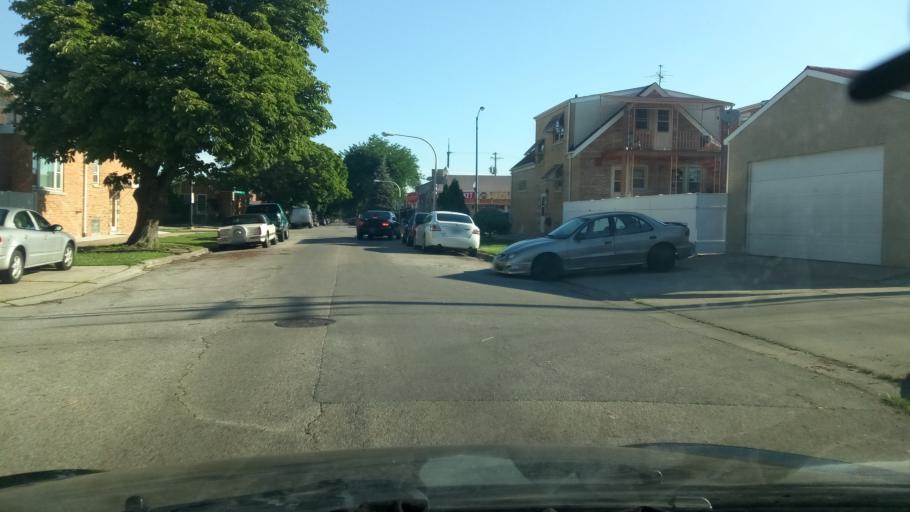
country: US
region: Illinois
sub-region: Cook County
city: Hometown
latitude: 41.7706
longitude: -87.7307
